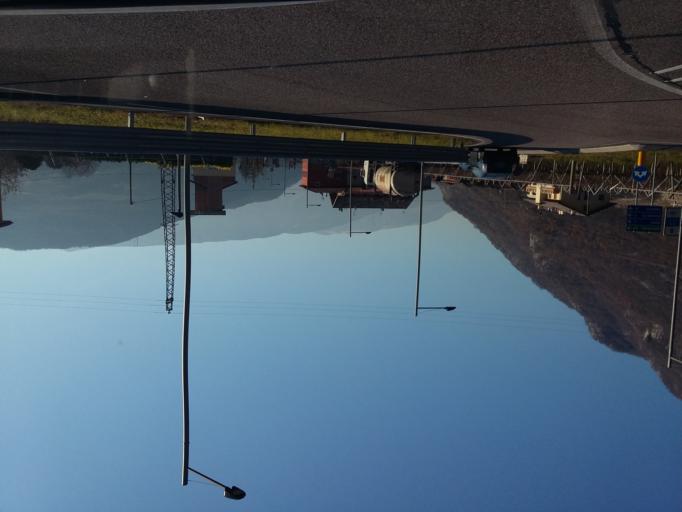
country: IT
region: Trentino-Alto Adige
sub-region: Provincia di Trento
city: Ronzo-Chienis
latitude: 45.8550
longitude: 10.9319
